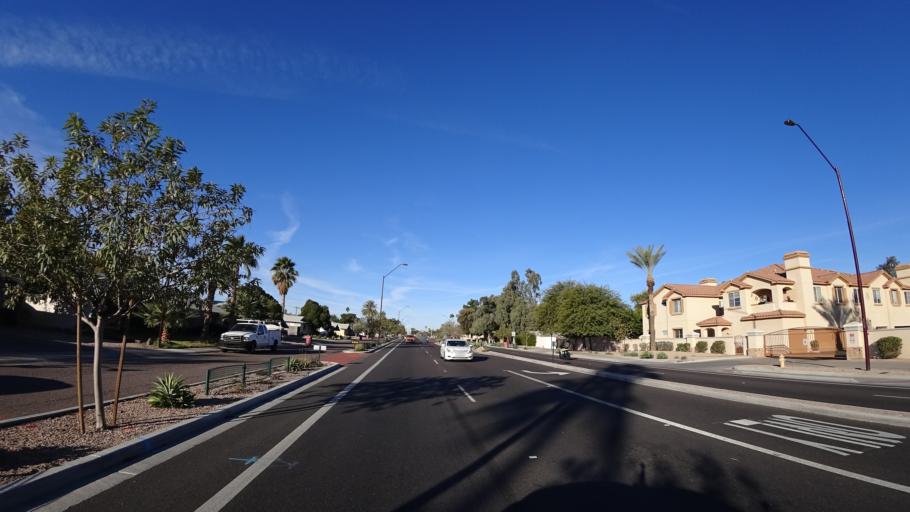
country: US
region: Arizona
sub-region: Maricopa County
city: Scottsdale
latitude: 33.4803
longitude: -111.9181
